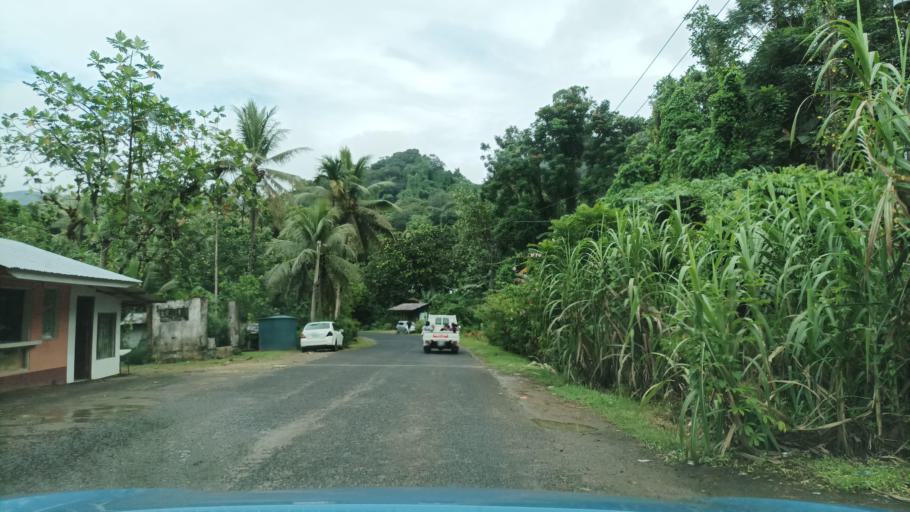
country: FM
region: Pohnpei
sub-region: Sokehs Municipality
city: Palikir - National Government Center
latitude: 6.8517
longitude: 158.1613
